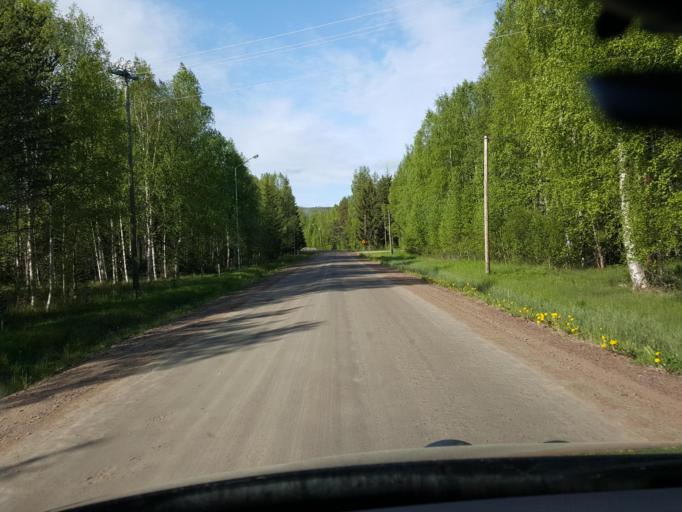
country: SE
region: Vaesternorrland
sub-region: Ange Kommun
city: Ange
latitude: 62.1826
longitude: 15.6358
